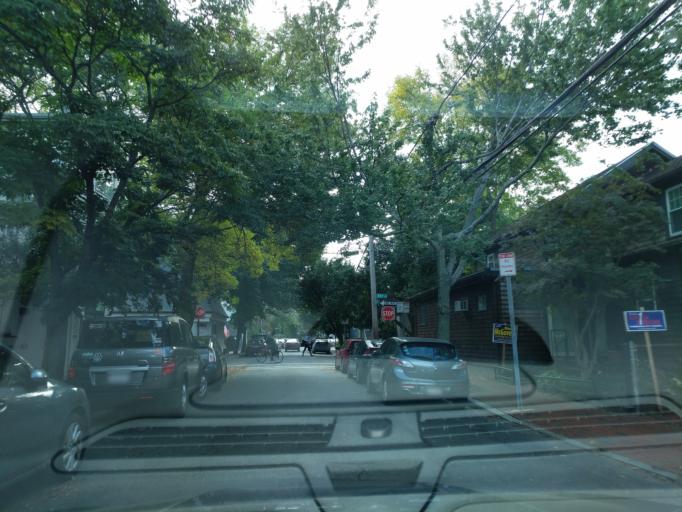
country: US
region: Massachusetts
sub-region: Middlesex County
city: Cambridge
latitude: 42.3679
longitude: -71.1115
